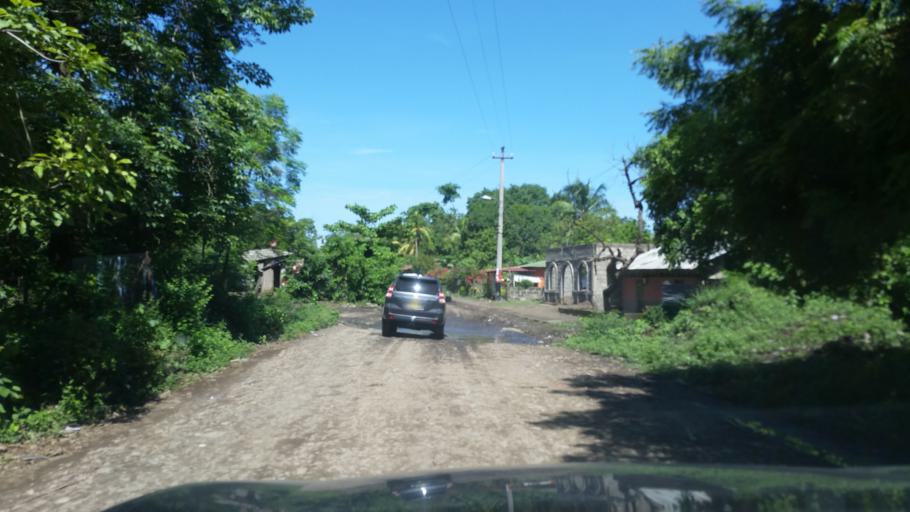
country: NI
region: Chinandega
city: Puerto Morazan
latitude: 12.7710
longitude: -87.1329
